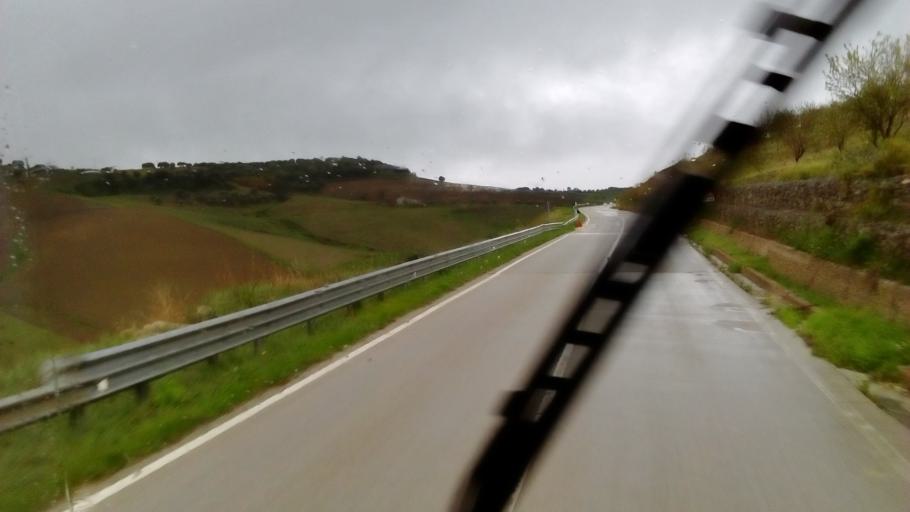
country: IT
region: Sicily
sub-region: Enna
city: Pietraperzia
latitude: 37.4400
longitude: 14.1768
